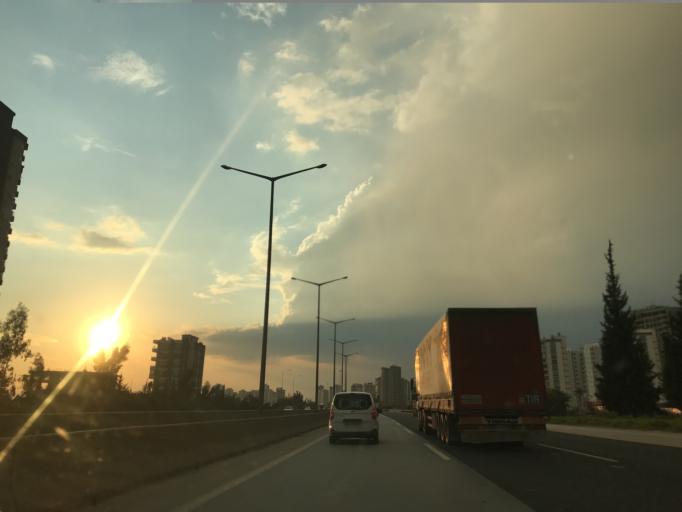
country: TR
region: Adana
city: Seyhan
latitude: 37.0323
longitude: 35.2586
